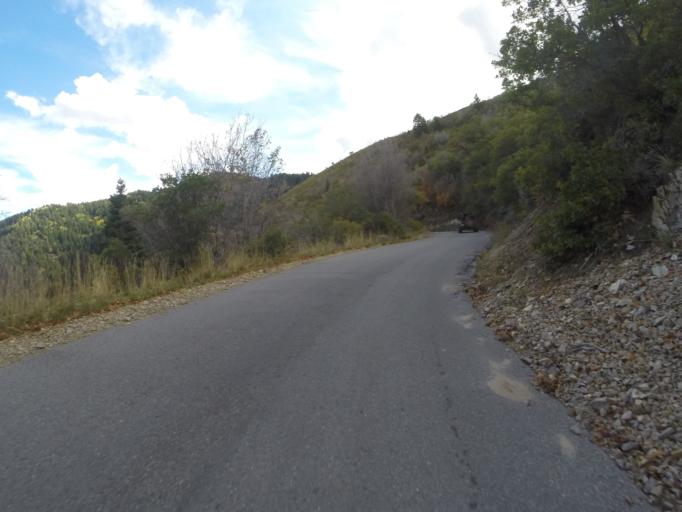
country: US
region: Utah
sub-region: Tooele County
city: Tooele
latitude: 40.4892
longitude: -112.1764
